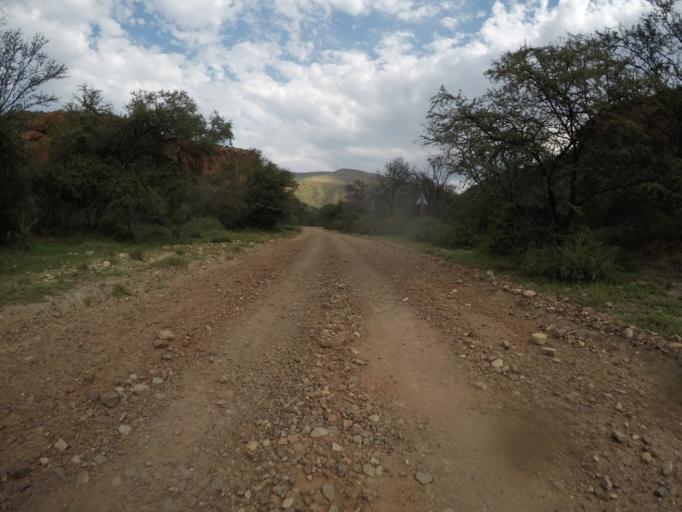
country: ZA
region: Eastern Cape
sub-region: Cacadu District Municipality
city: Kareedouw
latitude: -33.6007
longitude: 24.2077
